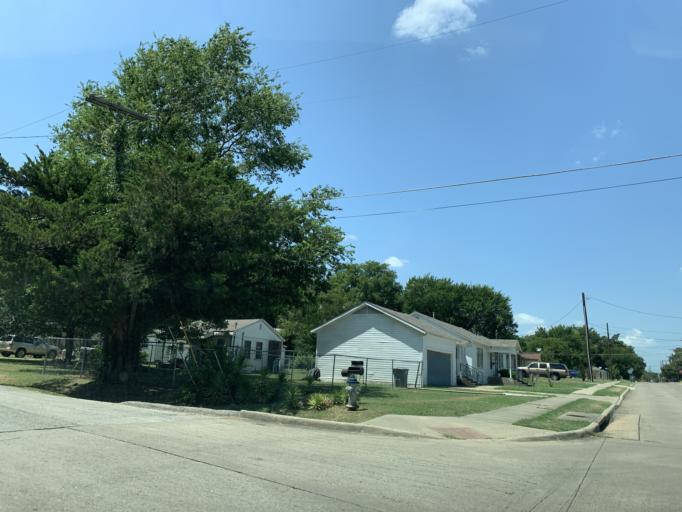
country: US
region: Texas
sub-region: Dallas County
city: Hutchins
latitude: 32.6874
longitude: -96.7781
